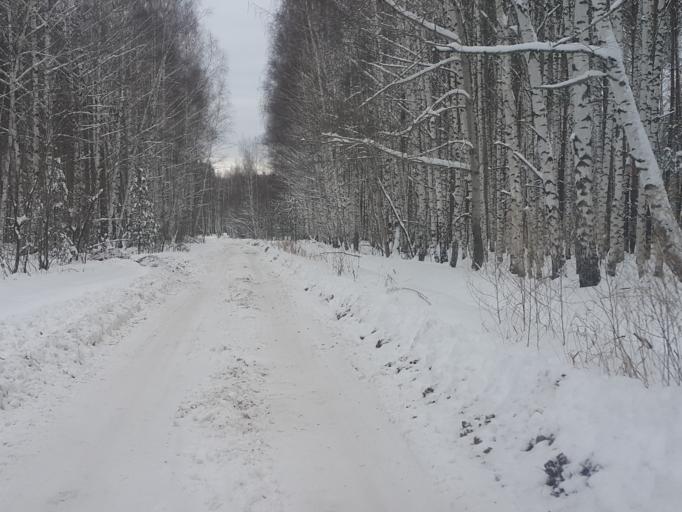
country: RU
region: Tambov
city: Platonovka
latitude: 52.8910
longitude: 41.8492
